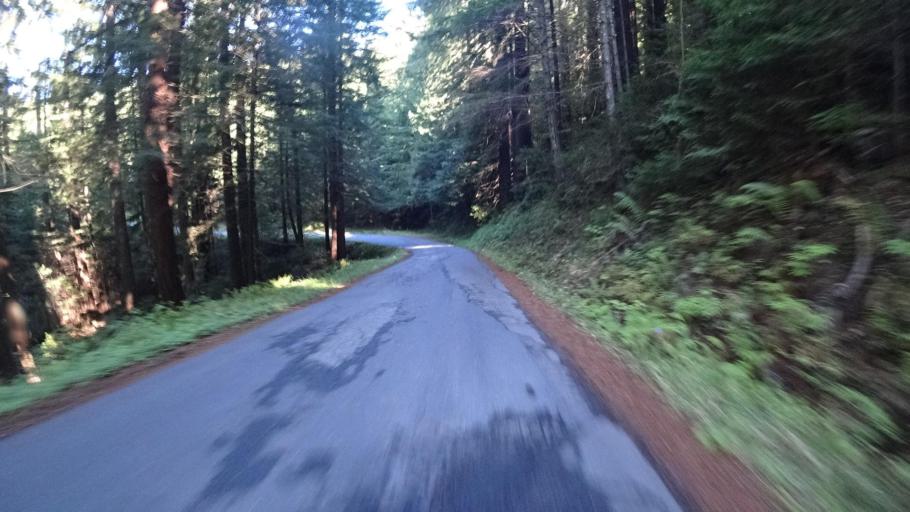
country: US
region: California
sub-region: Humboldt County
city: Rio Dell
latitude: 40.4600
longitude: -124.0035
